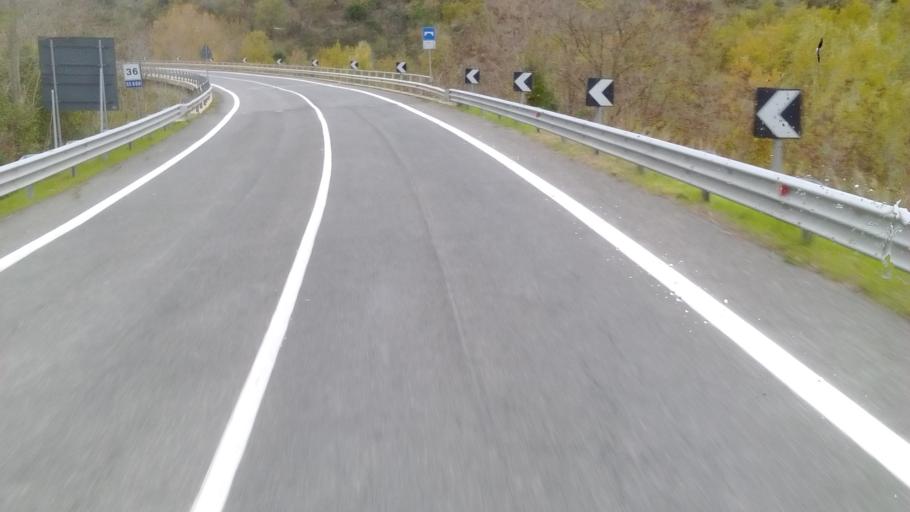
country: IT
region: Molise
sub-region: Provincia di Campobasso
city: Trivento
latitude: 41.7907
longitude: 14.5335
